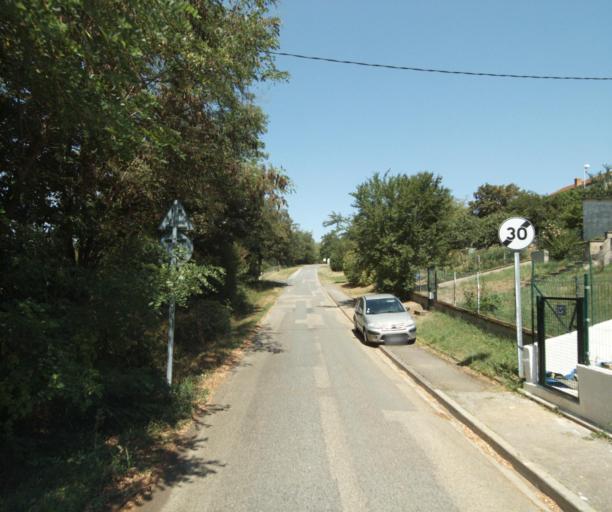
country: FR
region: Rhone-Alpes
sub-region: Departement du Rhone
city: Saint-Pierre-la-Palud
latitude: 45.7993
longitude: 4.6091
